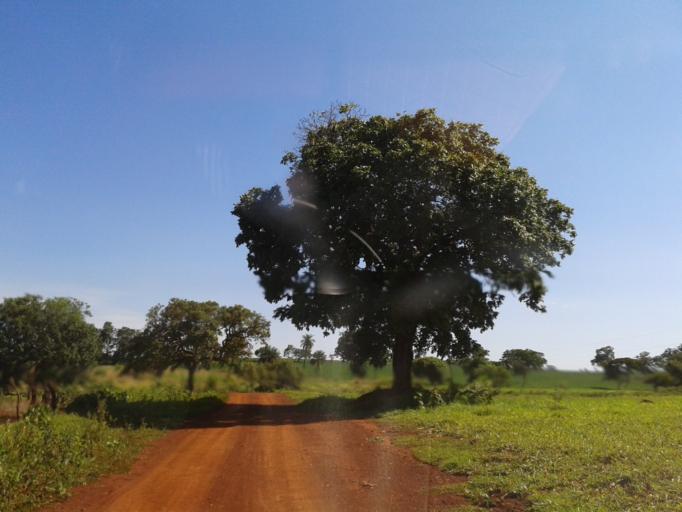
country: BR
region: Minas Gerais
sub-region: Centralina
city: Centralina
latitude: -18.6202
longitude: -49.2957
